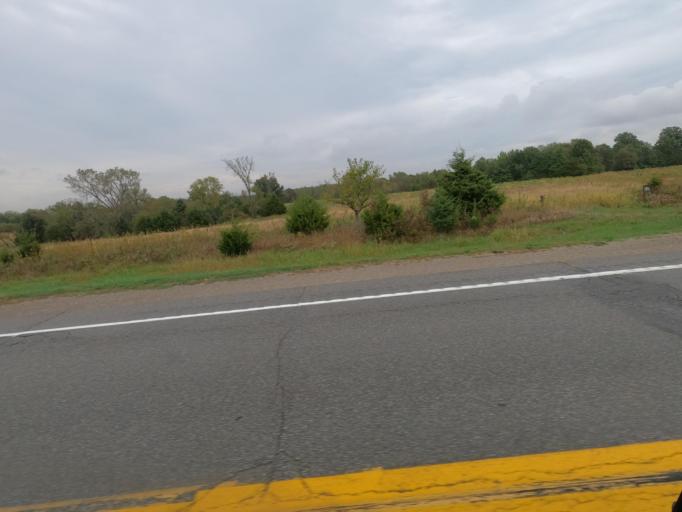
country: US
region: Iowa
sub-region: Van Buren County
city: Keosauqua
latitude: 40.8100
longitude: -91.9321
